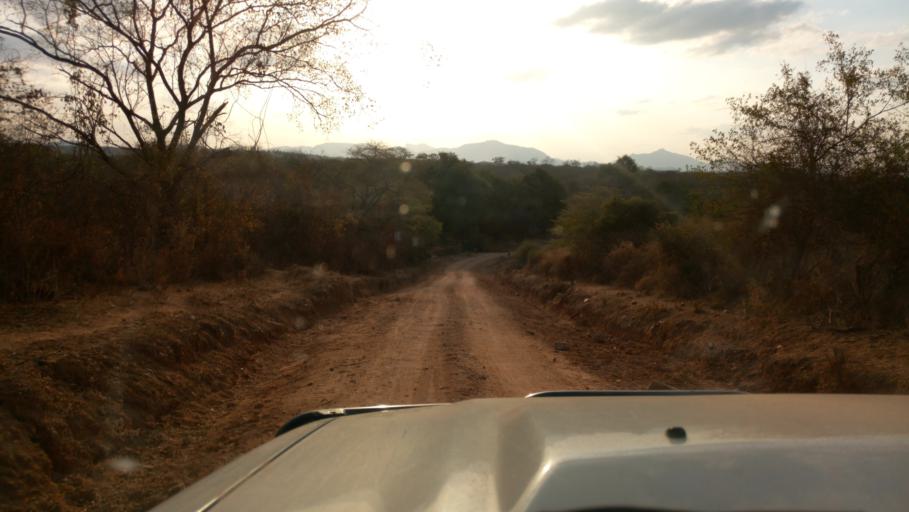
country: KE
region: Kitui
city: Kitui
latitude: -1.6414
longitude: 38.2955
